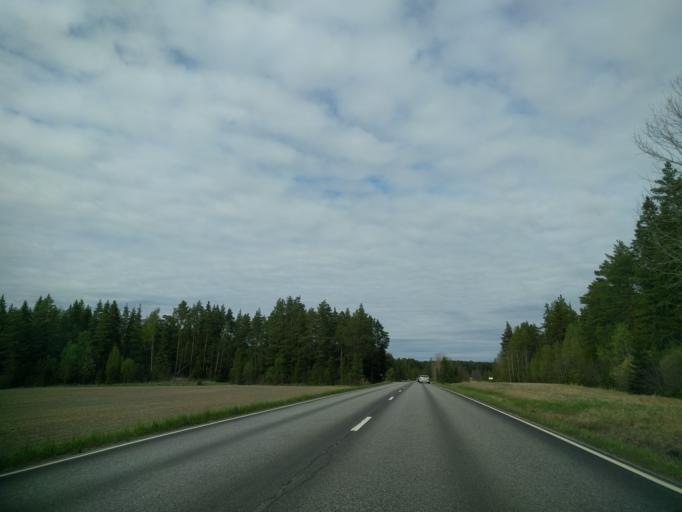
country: FI
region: Varsinais-Suomi
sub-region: Vakka-Suomi
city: Taivassalo
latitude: 60.5874
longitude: 21.6493
